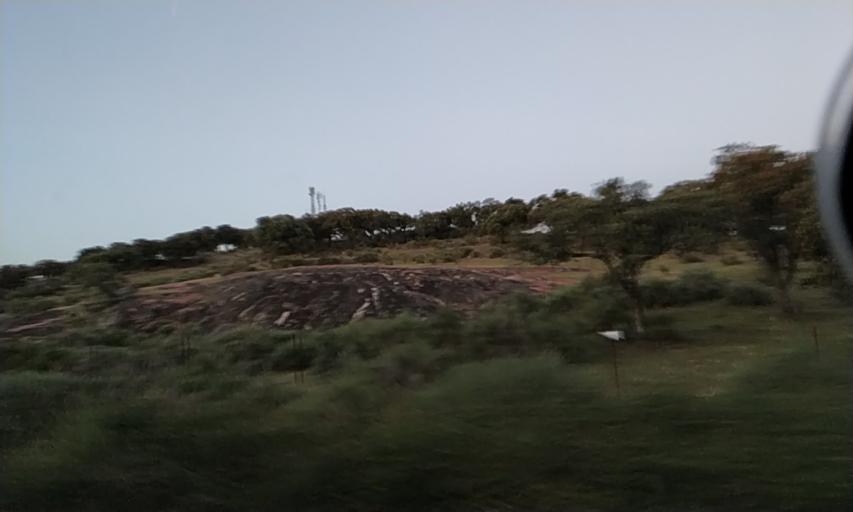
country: ES
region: Extremadura
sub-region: Provincia de Caceres
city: Alcantara
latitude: 39.7466
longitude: -6.9026
